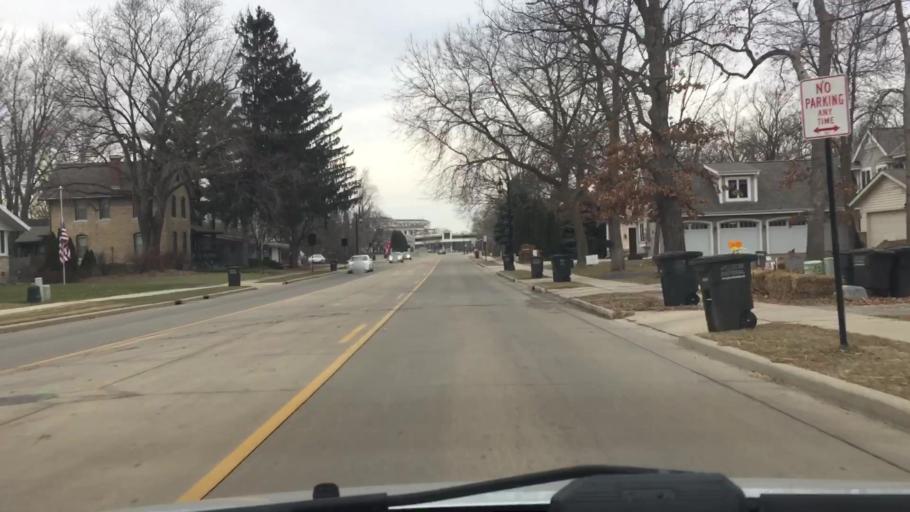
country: US
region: Wisconsin
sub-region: Waukesha County
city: Oconomowoc
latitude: 43.1172
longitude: -88.5172
